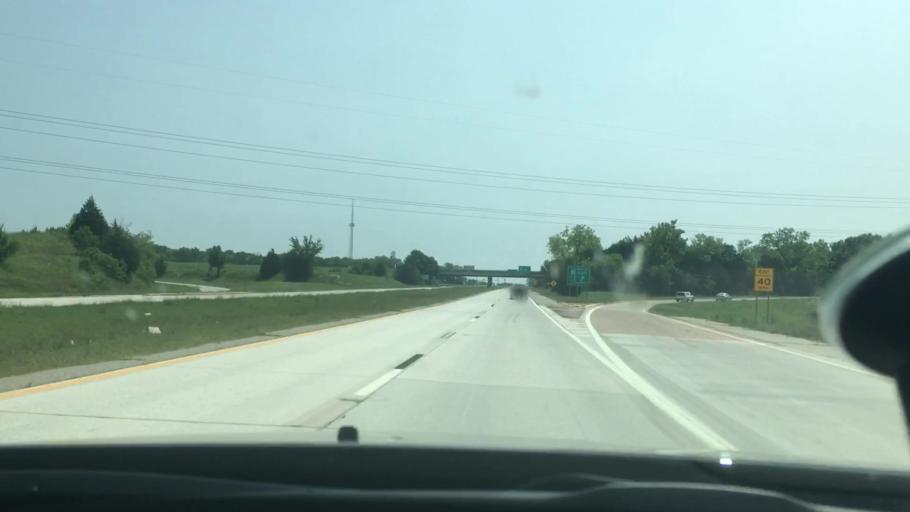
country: US
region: Oklahoma
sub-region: Pontotoc County
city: Ada
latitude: 34.7777
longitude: -96.7061
